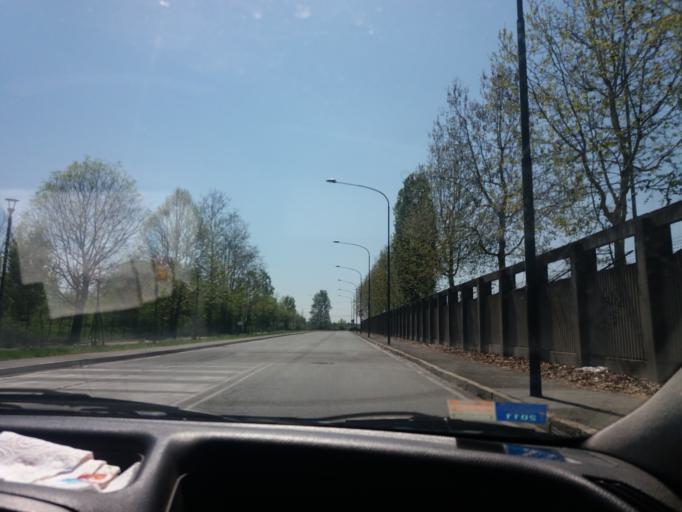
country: IT
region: Piedmont
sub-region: Provincia di Torino
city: Fornaci
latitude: 45.0197
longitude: 7.6045
